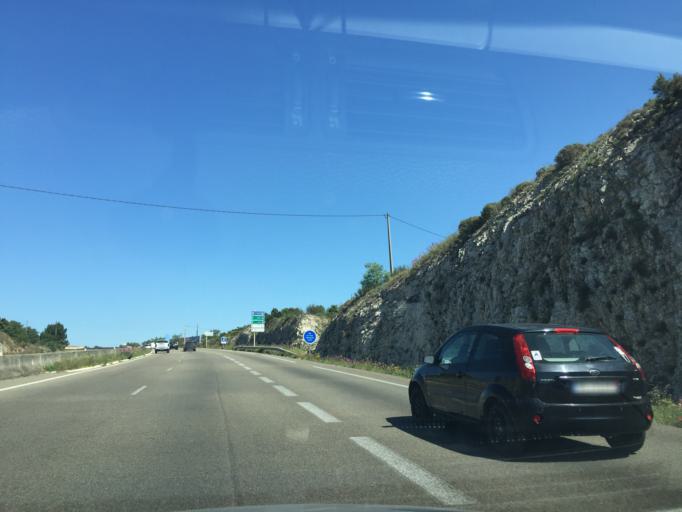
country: FR
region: Languedoc-Roussillon
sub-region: Departement du Gard
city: Les Angles
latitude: 43.9549
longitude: 4.7564
